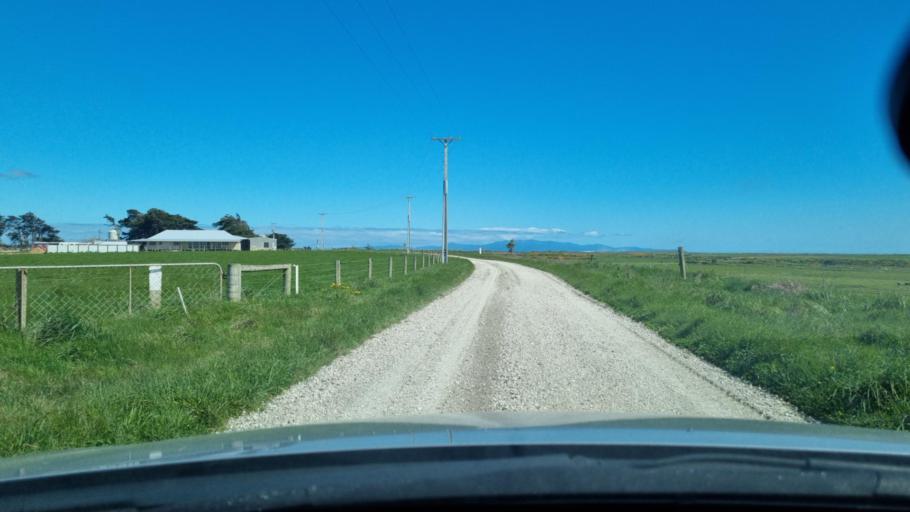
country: NZ
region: Southland
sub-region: Invercargill City
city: Invercargill
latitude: -46.3984
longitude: 168.2570
